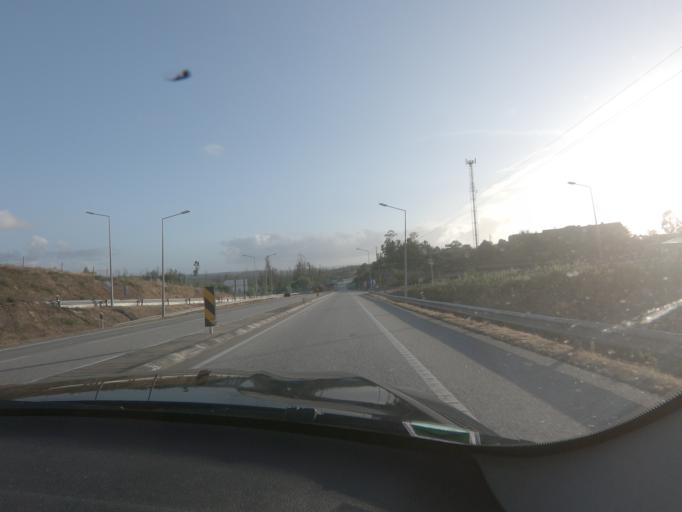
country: PT
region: Viseu
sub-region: Santa Comba Dao
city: Santa Comba Dao
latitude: 40.3537
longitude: -8.1538
